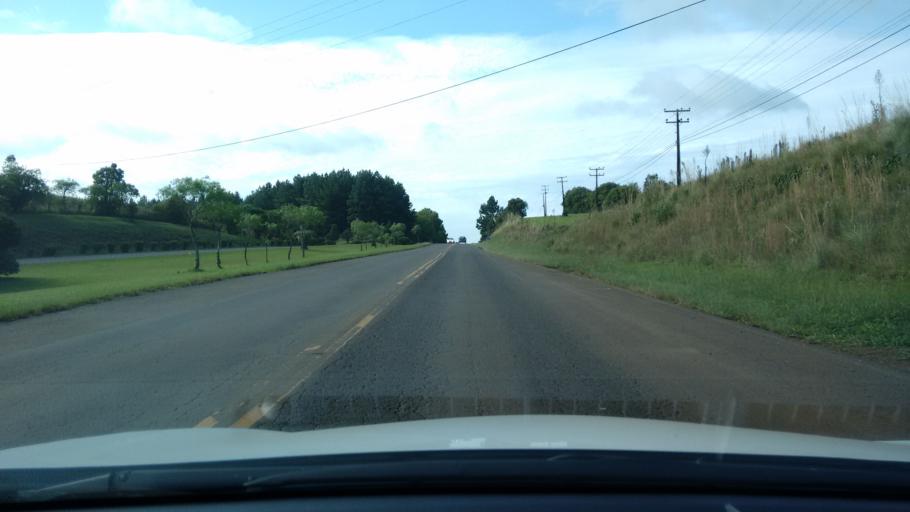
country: BR
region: Santa Catarina
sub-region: Videira
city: Videira
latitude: -27.0568
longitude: -50.8977
